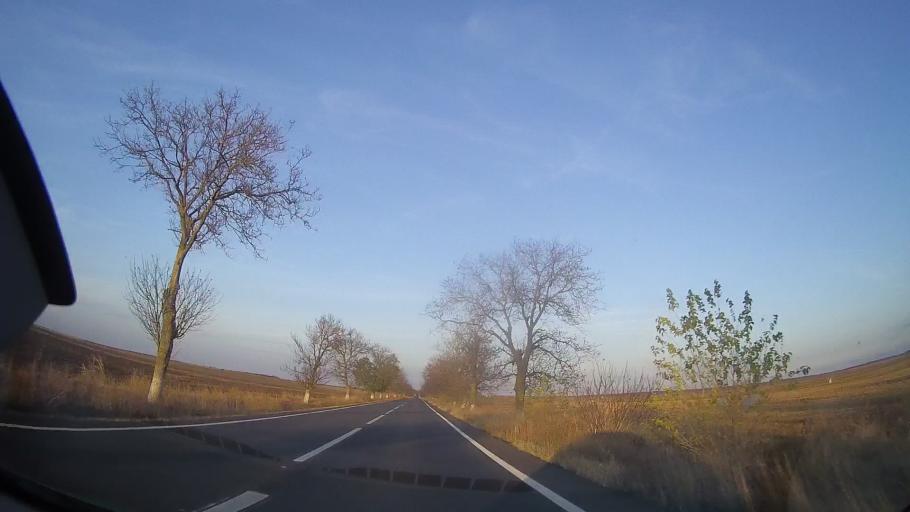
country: RO
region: Constanta
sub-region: Comuna Amzacea
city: Amzacea
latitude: 43.9410
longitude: 28.3713
